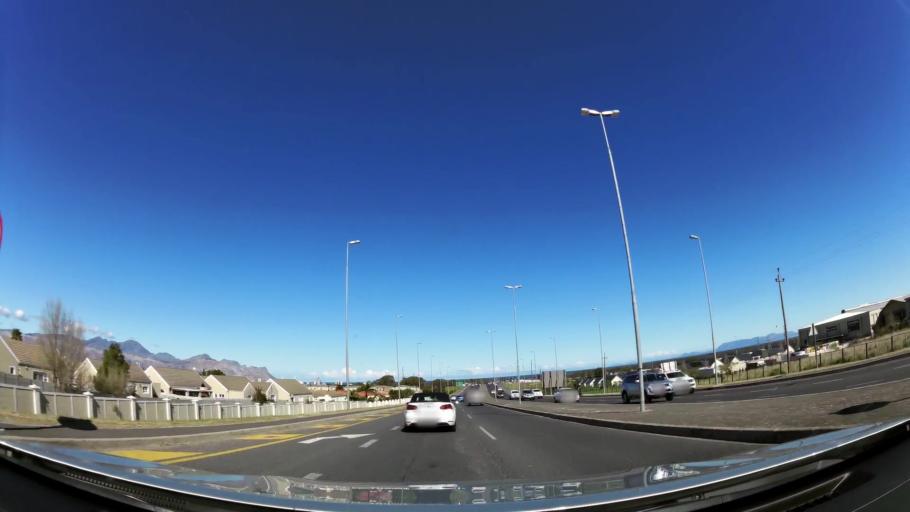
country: ZA
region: Western Cape
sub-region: Cape Winelands District Municipality
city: Stellenbosch
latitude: -34.0712
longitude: 18.8246
